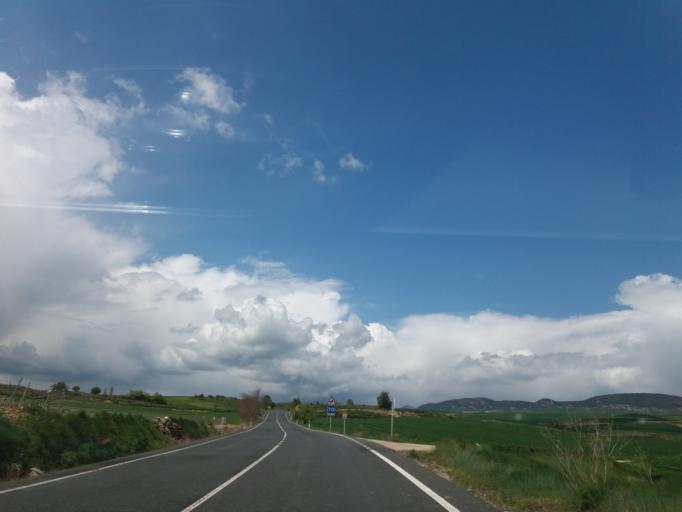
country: ES
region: La Rioja
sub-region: Provincia de La Rioja
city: Fonzaleche
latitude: 42.5744
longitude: -3.0142
